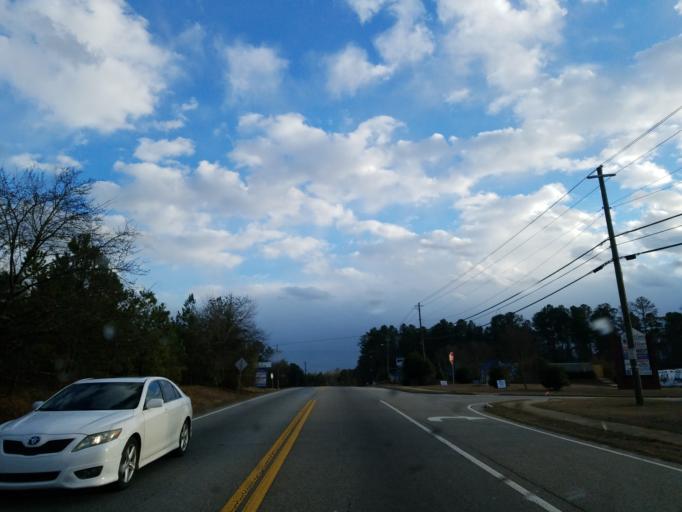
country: US
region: Georgia
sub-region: Henry County
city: Stockbridge
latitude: 33.5292
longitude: -84.1976
